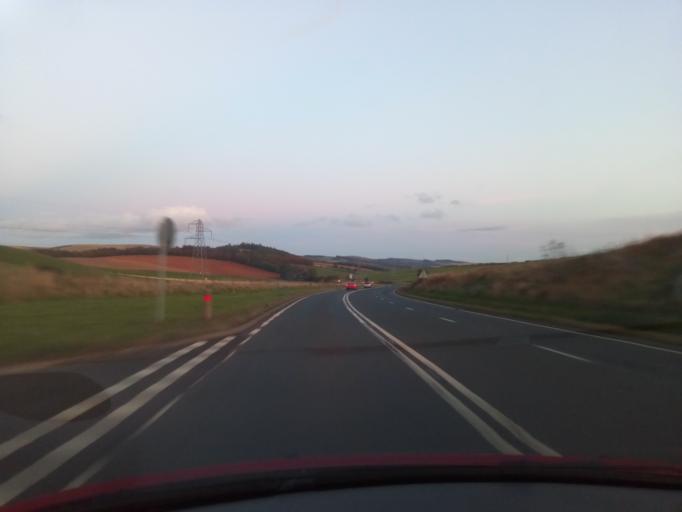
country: GB
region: Scotland
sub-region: The Scottish Borders
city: Lauder
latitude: 55.7870
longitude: -2.8247
